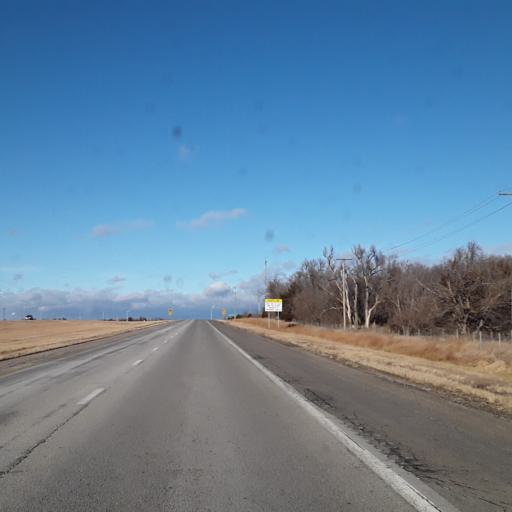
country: US
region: Kansas
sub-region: Republic County
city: Belleville
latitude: 39.8357
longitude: -97.6348
